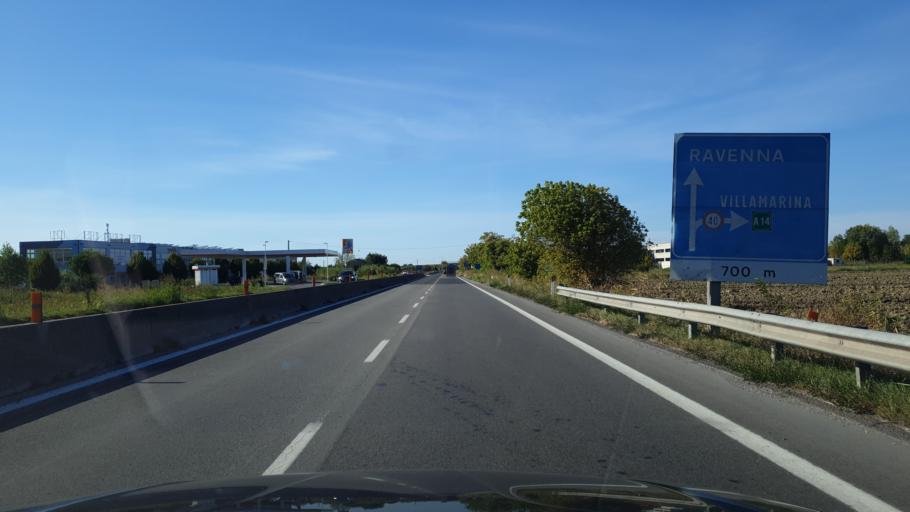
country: IT
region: Emilia-Romagna
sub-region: Forli-Cesena
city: Gatteo a Mare
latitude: 44.1742
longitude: 12.4177
